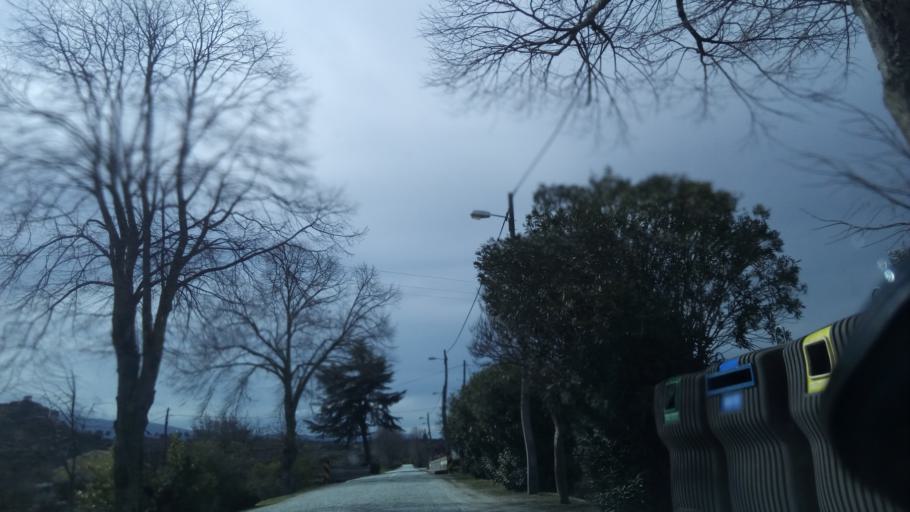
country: PT
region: Guarda
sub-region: Fornos de Algodres
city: Fornos de Algodres
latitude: 40.5864
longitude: -7.5399
